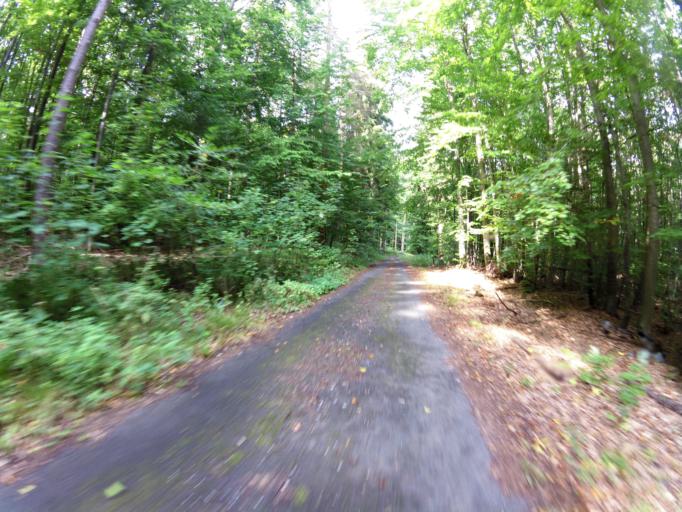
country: DE
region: Bavaria
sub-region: Regierungsbezirk Unterfranken
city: Waldbrunn
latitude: 49.7248
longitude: 9.7978
